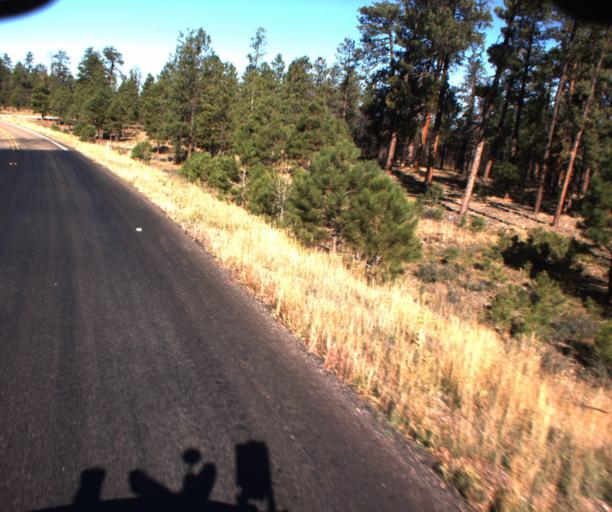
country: US
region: Arizona
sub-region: Coconino County
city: Fredonia
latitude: 36.7426
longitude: -112.2316
